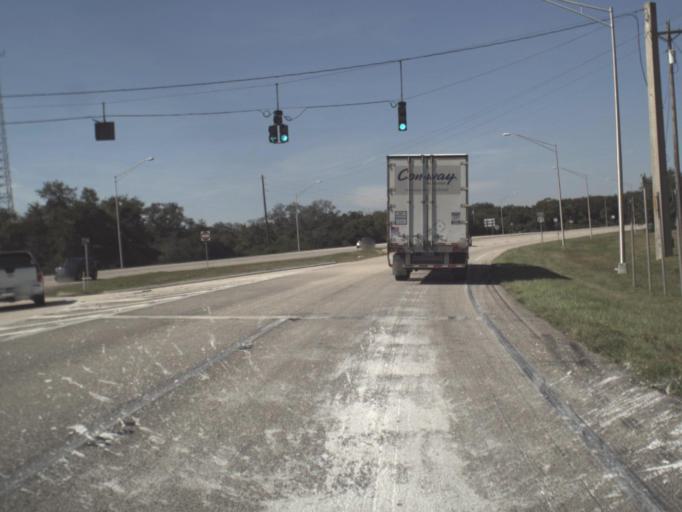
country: US
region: Florida
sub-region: Hendry County
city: Port LaBelle
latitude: 26.9251
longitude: -81.3114
